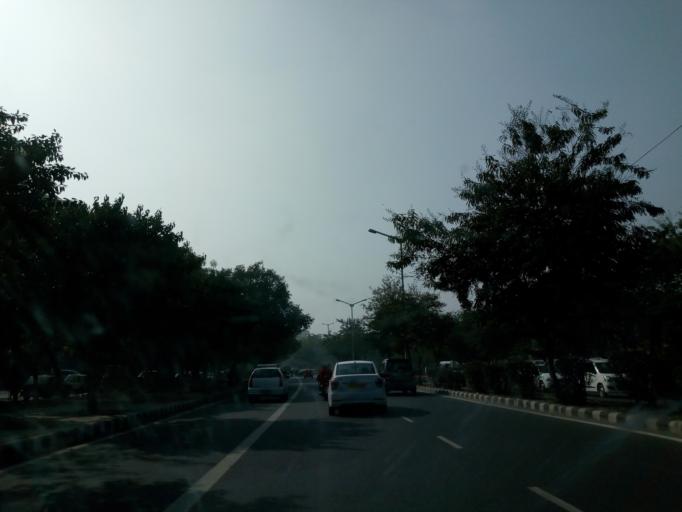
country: IN
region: NCT
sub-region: West Delhi
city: Nangloi Jat
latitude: 28.6051
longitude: 77.0487
